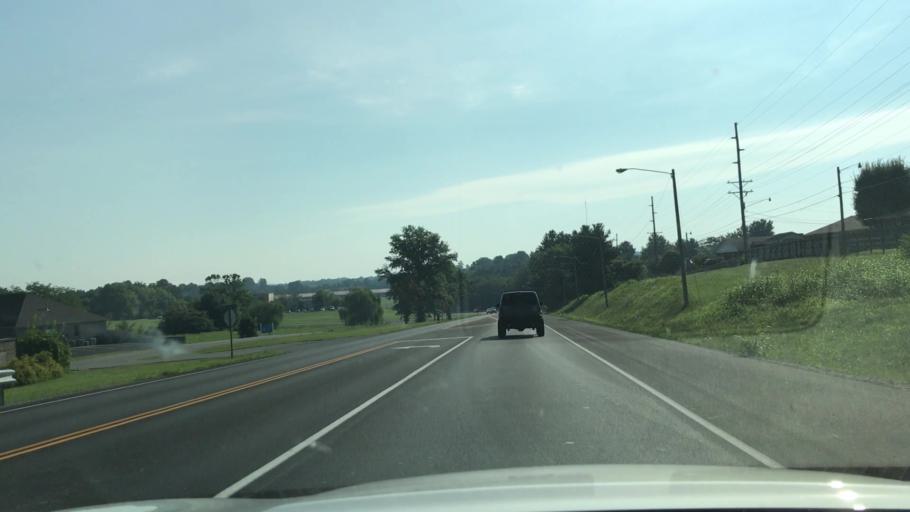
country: US
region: Kentucky
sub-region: Barren County
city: Glasgow
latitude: 37.0152
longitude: -85.9128
